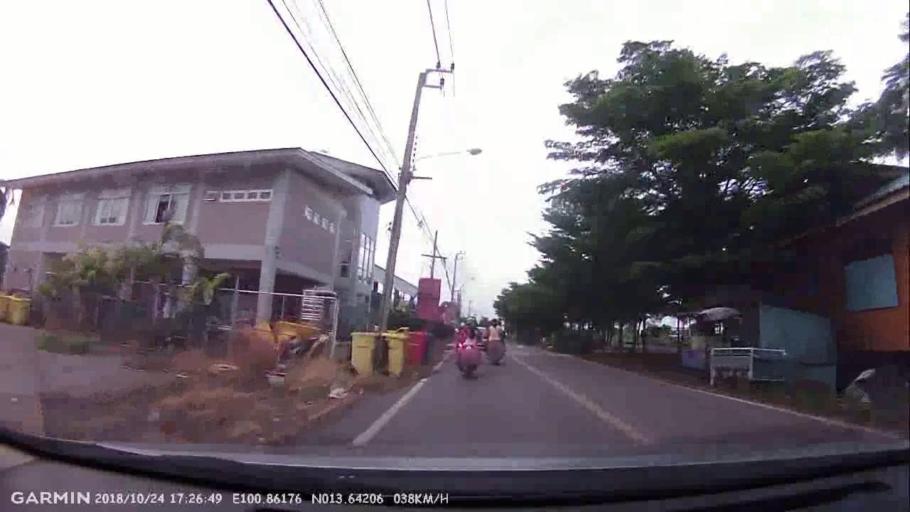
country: TH
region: Samut Prakan
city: Ban Khlong Bang Sao Thong
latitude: 13.6421
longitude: 100.8617
